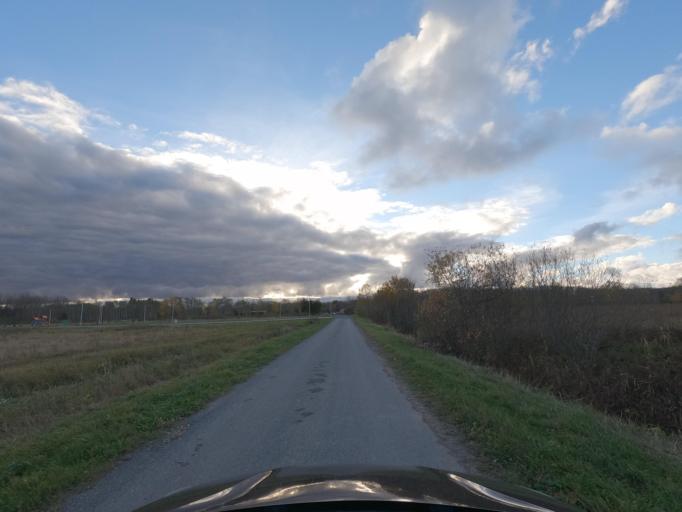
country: EE
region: Harju
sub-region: Saue vald
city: Laagri
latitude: 59.3676
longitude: 24.5678
